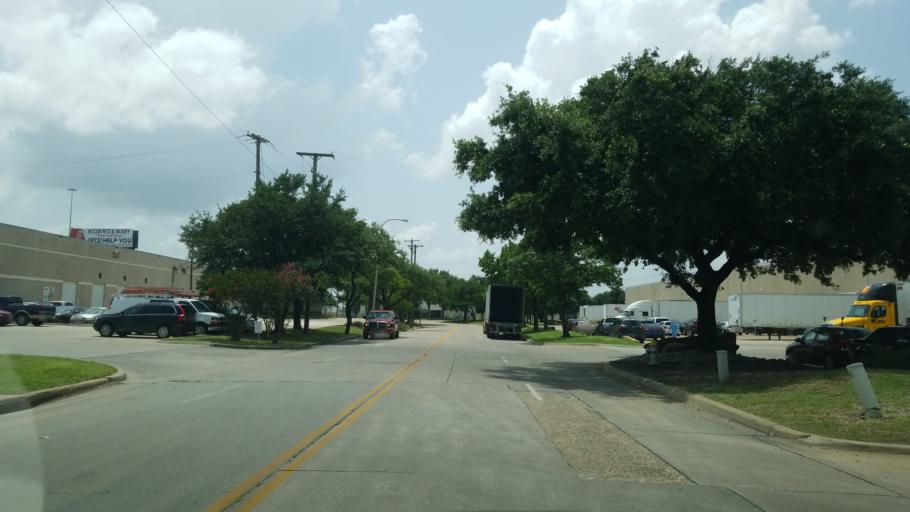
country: US
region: Texas
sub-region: Dallas County
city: Cockrell Hill
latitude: 32.7692
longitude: -96.8823
